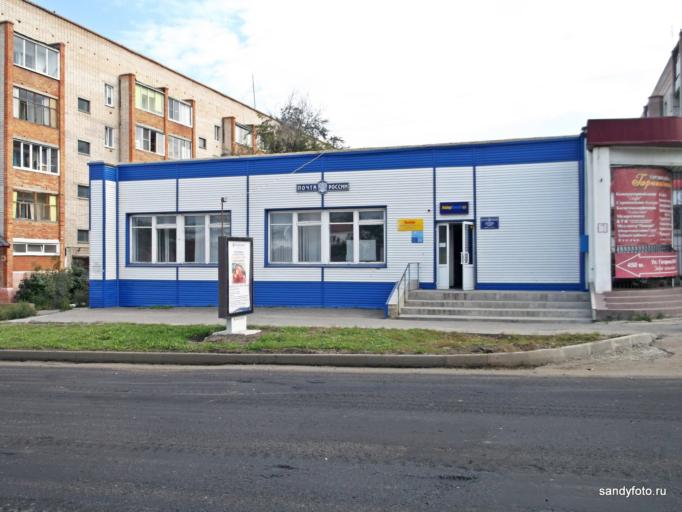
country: RU
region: Chelyabinsk
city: Troitsk
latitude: 54.0833
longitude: 61.5407
